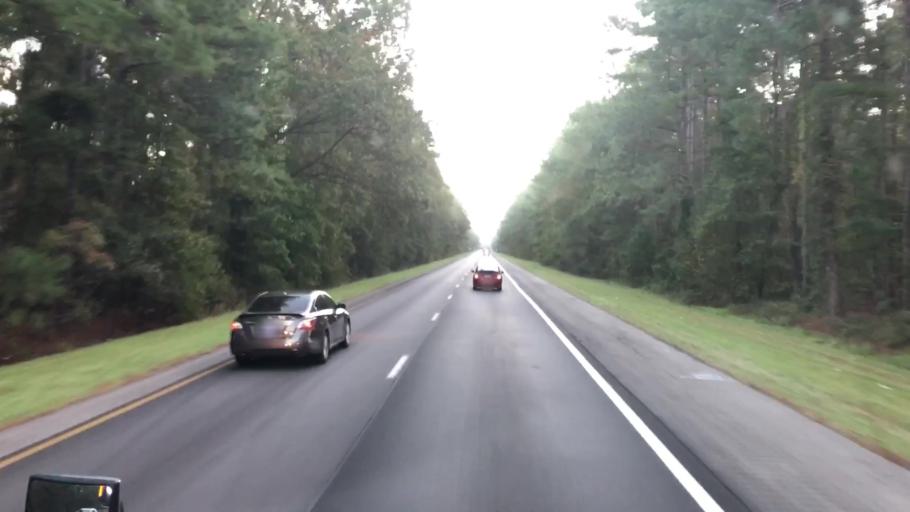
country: US
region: South Carolina
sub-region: Clarendon County
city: Manning
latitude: 33.5574
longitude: -80.3998
